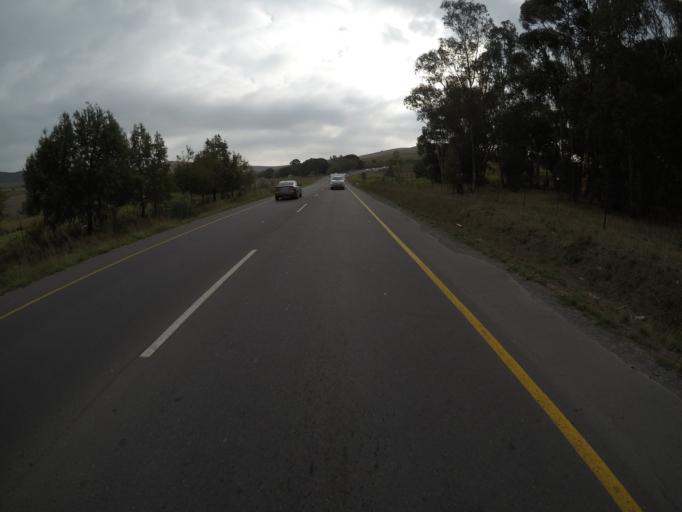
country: ZA
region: Western Cape
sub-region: City of Cape Town
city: Sunset Beach
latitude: -33.8387
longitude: 18.5969
